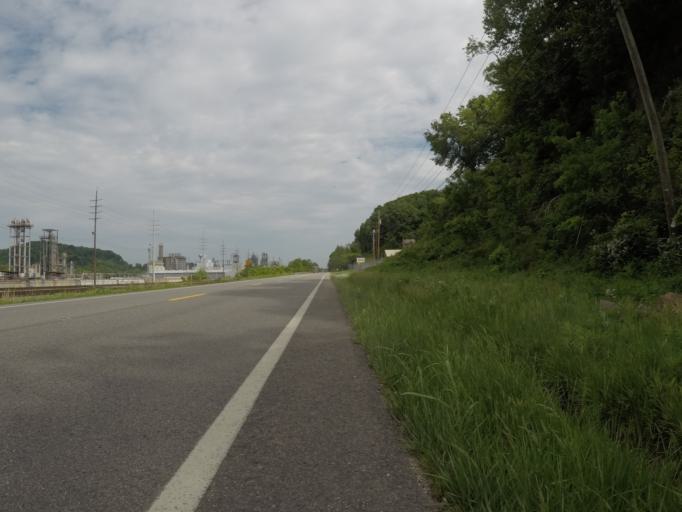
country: US
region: West Virginia
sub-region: Wayne County
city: Kenova
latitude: 38.3506
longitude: -82.5934
